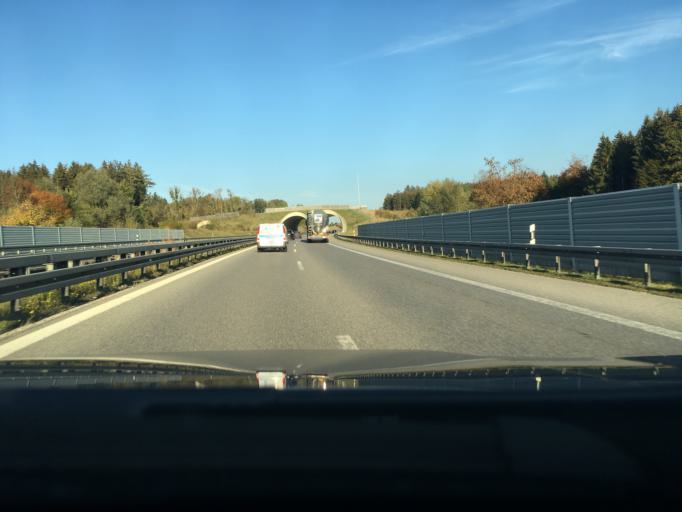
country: DE
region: Baden-Wuerttemberg
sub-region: Tuebingen Region
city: Kisslegg
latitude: 47.7750
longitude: 9.9372
